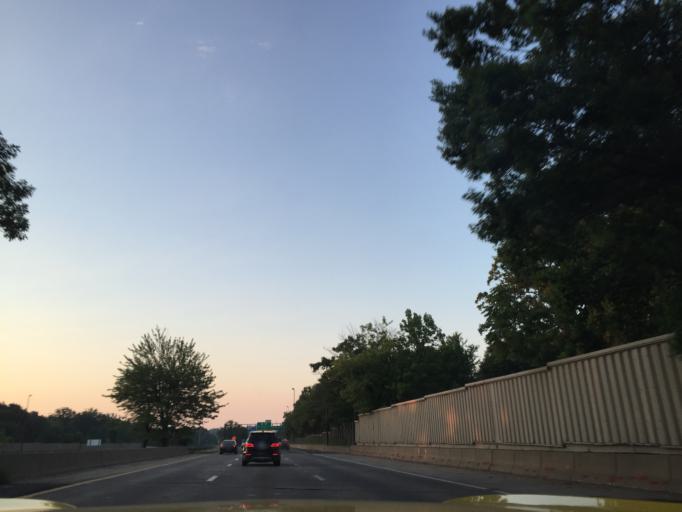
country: US
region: Virginia
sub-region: City of Falls Church
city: Falls Church
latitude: 38.8943
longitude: -77.1697
